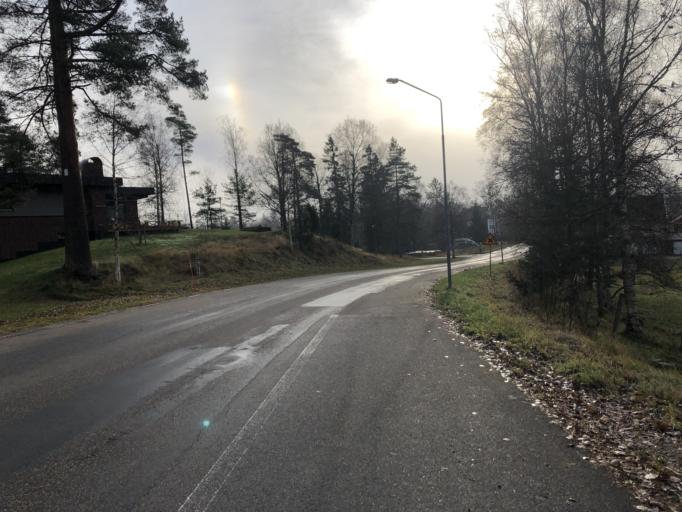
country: SE
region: Vaestra Goetaland
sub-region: Ulricehamns Kommun
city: Ulricehamn
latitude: 57.6965
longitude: 13.5718
